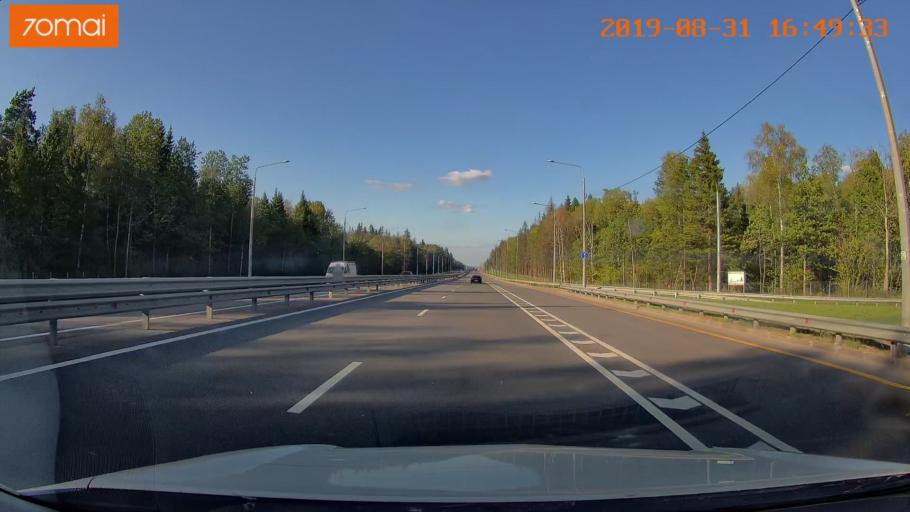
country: RU
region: Kaluga
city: Pyatovskiy
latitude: 54.6924
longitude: 36.1556
